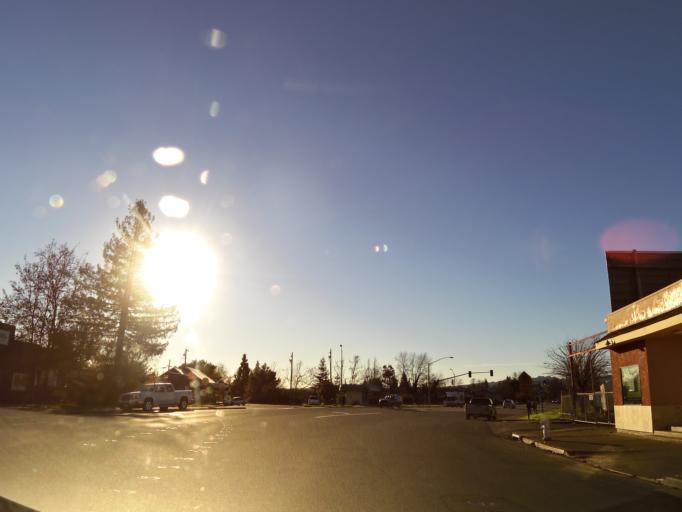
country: US
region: California
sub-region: Sonoma County
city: Cloverdale
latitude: 38.8038
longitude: -123.0162
